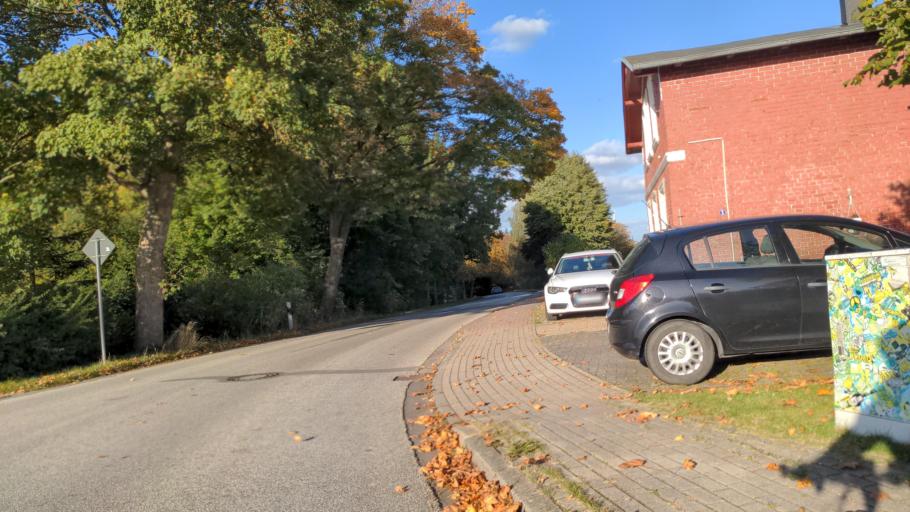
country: DE
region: Schleswig-Holstein
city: Monkhagen
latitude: 53.9235
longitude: 10.5251
